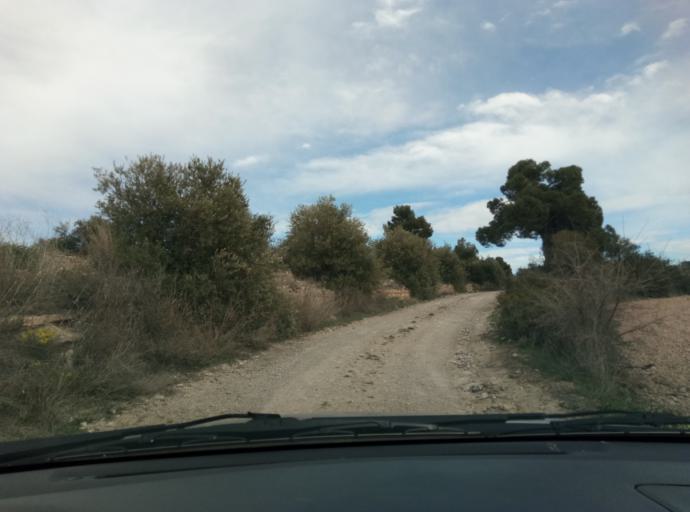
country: ES
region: Catalonia
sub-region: Provincia de Lleida
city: Ciutadilla
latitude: 41.5786
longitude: 1.1180
